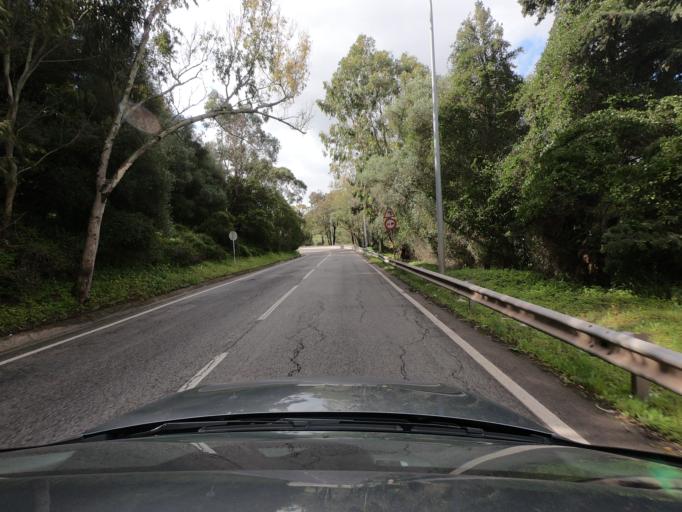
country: PT
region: Lisbon
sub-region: Oeiras
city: Carnaxide
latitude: 38.7271
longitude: -9.2565
